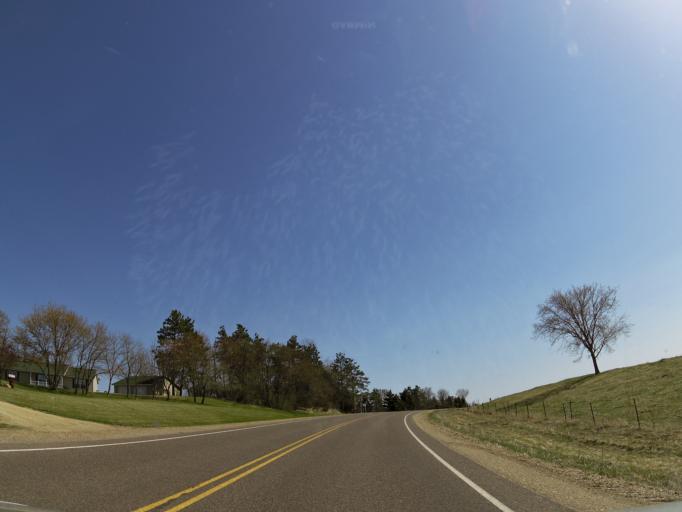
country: US
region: Wisconsin
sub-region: Saint Croix County
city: Baldwin
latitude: 44.8681
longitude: -92.4159
